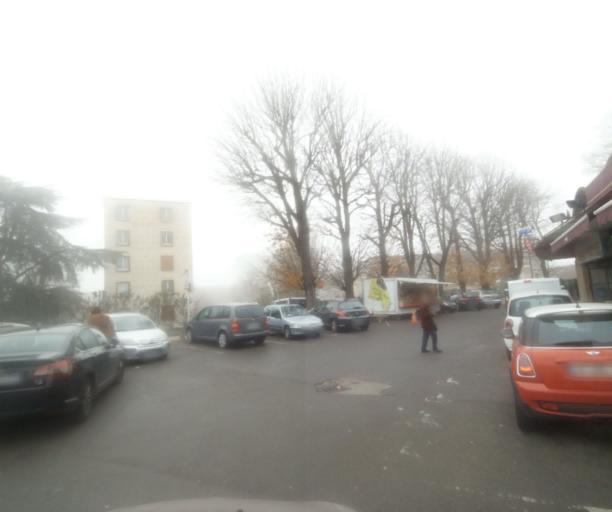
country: FR
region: Ile-de-France
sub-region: Departement de Seine-Saint-Denis
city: Clichy-sous-Bois
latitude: 48.9096
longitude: 2.5503
